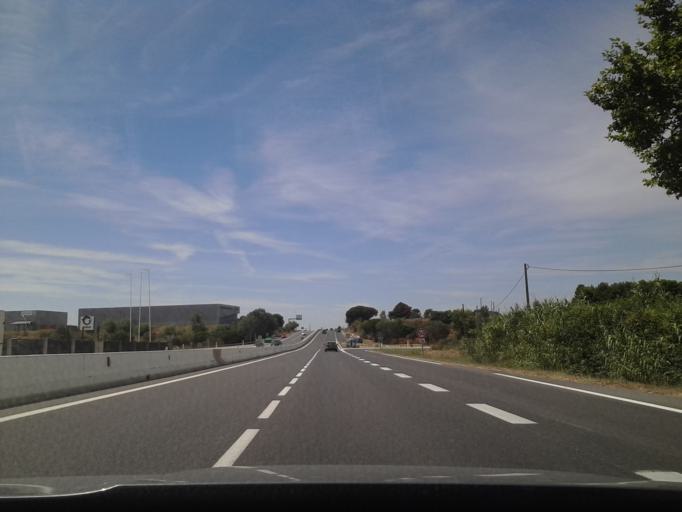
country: FR
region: Languedoc-Roussillon
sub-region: Departement des Pyrenees-Orientales
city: Pia
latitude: 42.7560
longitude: 2.8963
